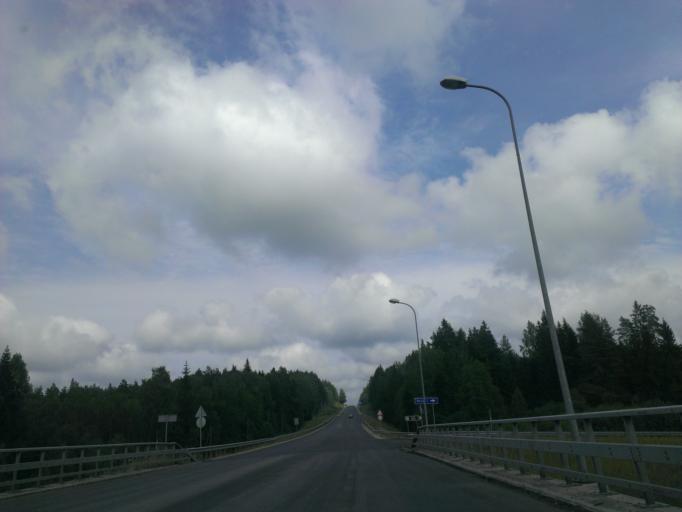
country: LV
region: Amatas Novads
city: Drabesi
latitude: 57.2222
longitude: 25.2348
